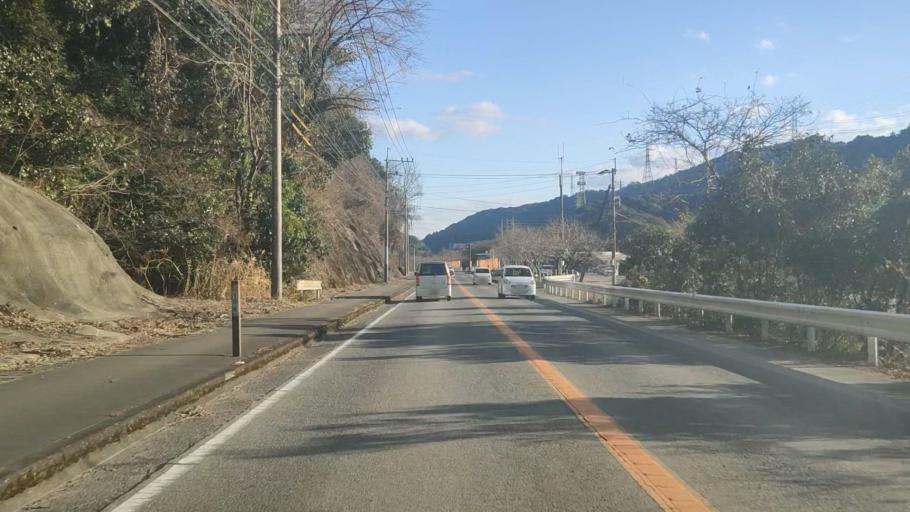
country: JP
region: Saga Prefecture
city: Saga-shi
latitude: 33.3413
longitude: 130.2565
